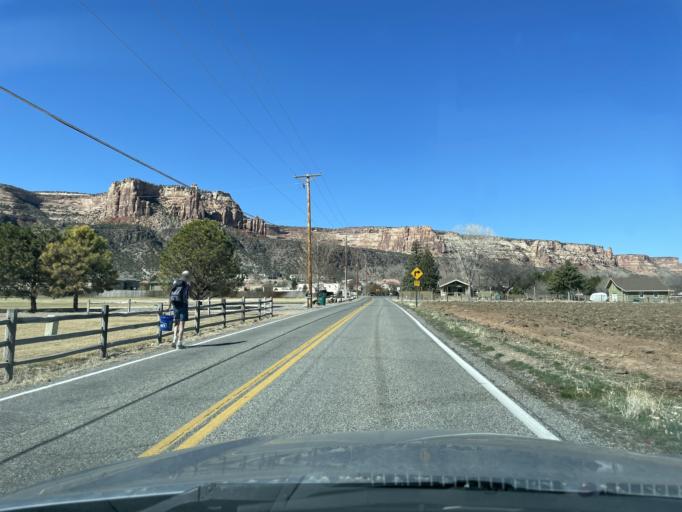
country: US
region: Colorado
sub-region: Mesa County
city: Redlands
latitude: 39.0742
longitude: -108.6619
